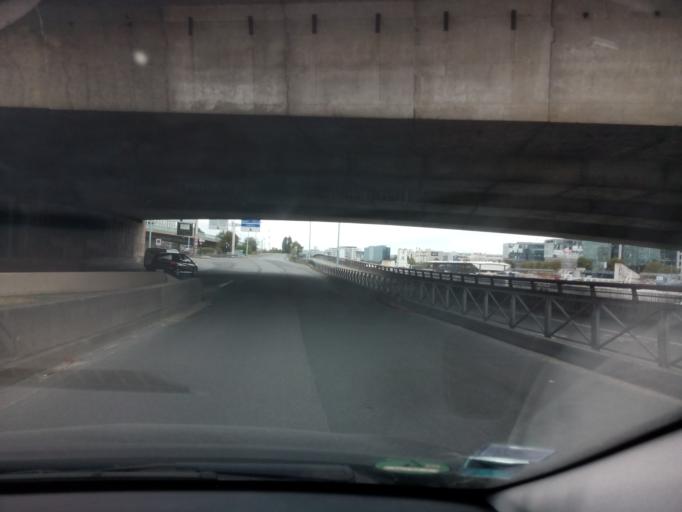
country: FR
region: Ile-de-France
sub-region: Departement du Val-de-Marne
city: Ivry-sur-Seine
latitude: 48.8272
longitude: 2.3897
